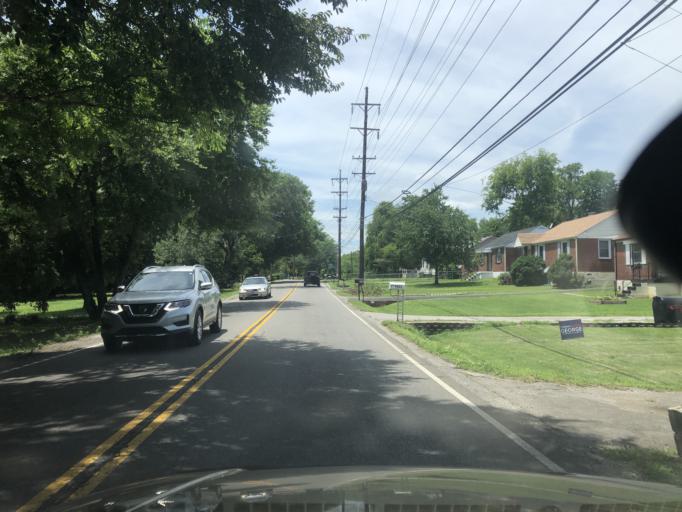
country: US
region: Tennessee
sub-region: Davidson County
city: Lakewood
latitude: 36.2536
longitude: -86.6991
